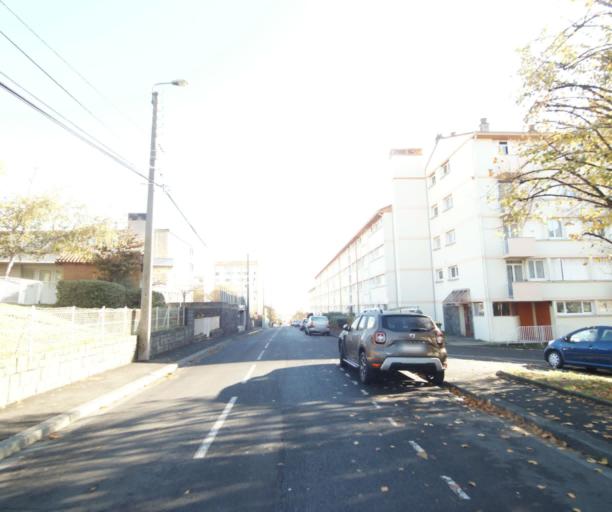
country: FR
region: Auvergne
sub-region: Departement du Puy-de-Dome
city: Clermont-Ferrand
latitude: 45.7935
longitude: 3.0748
